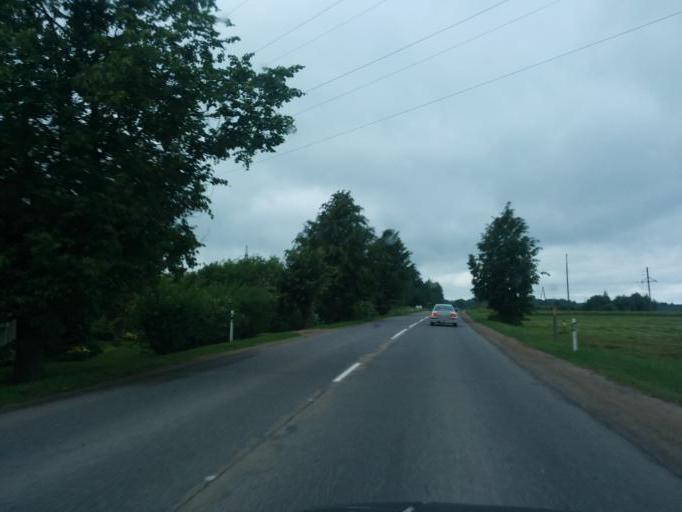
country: LV
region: Smiltene
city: Smiltene
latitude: 57.4316
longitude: 25.8825
